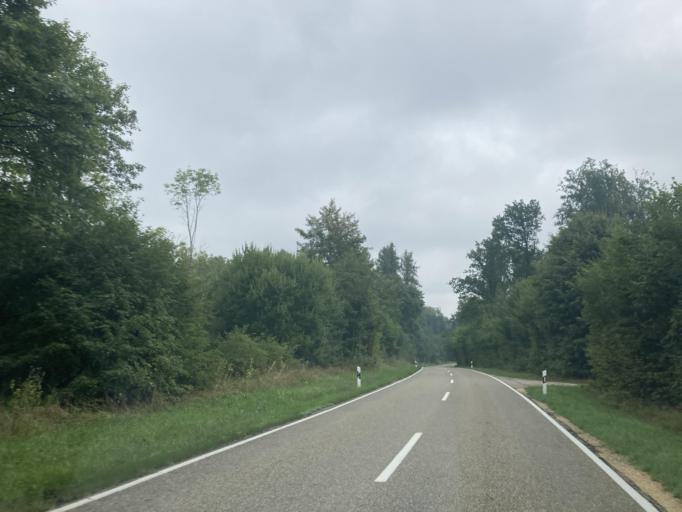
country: DE
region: Bavaria
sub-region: Swabia
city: Medlingen
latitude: 48.5898
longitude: 10.3097
